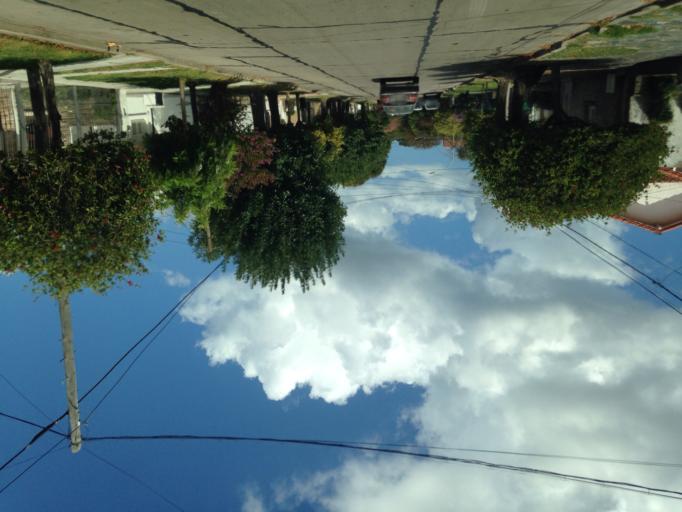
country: AR
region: Buenos Aires
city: Mar del Plata
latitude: -38.0188
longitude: -57.5596
